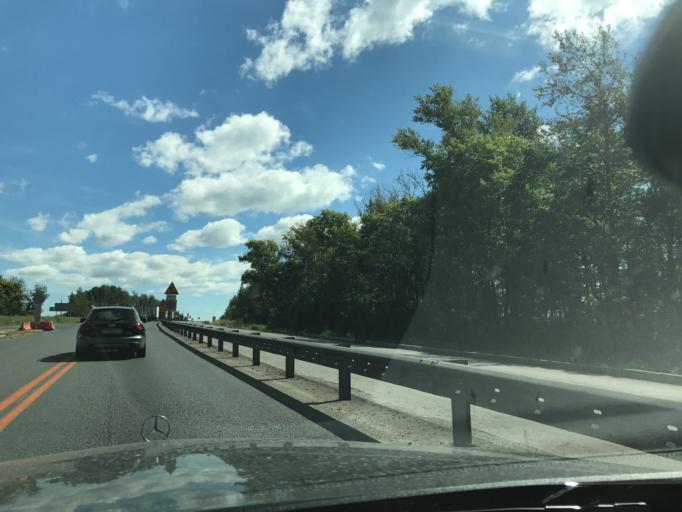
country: RU
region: Vladimir
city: Novovyazniki
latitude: 56.2155
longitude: 42.2511
